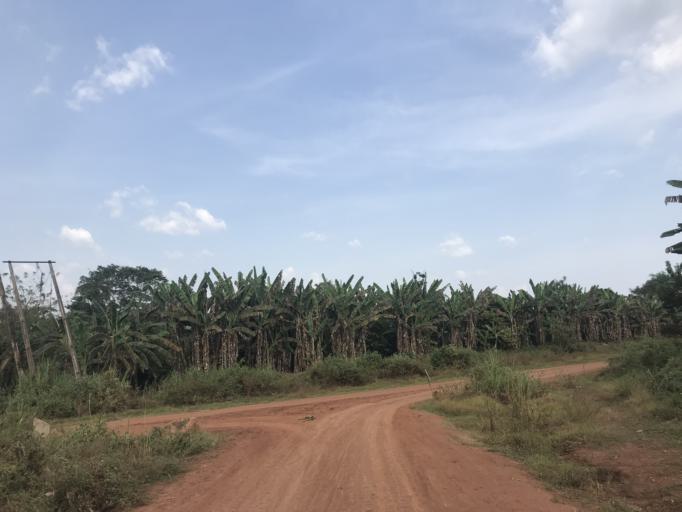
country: NG
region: Osun
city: Ilesa
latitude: 7.6592
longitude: 4.6727
